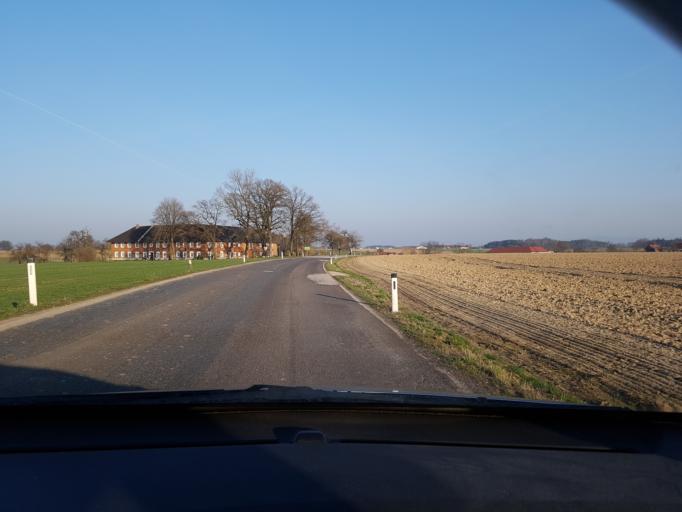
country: AT
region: Upper Austria
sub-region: Politischer Bezirk Linz-Land
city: Ansfelden
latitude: 48.1312
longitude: 14.2904
